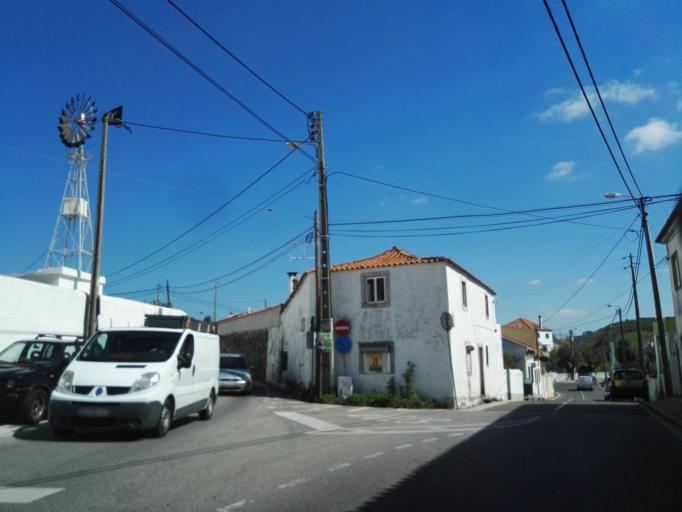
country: PT
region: Lisbon
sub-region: Sintra
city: Rio de Mouro
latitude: 38.7598
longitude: -9.3296
